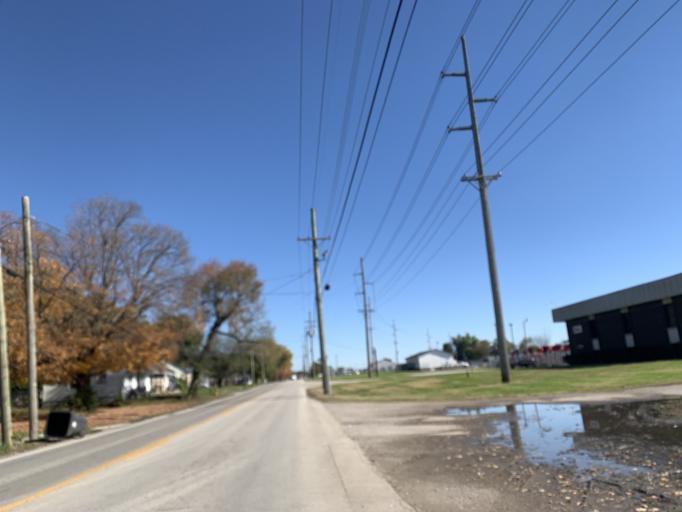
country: US
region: Kentucky
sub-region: Jefferson County
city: Shively
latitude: 38.2218
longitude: -85.8178
